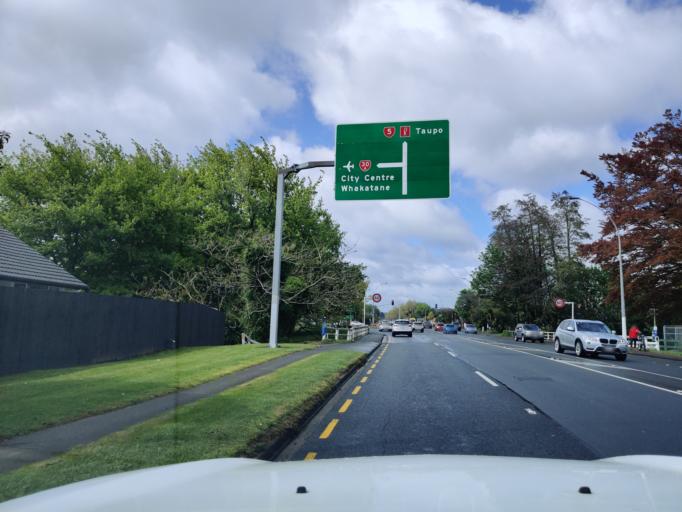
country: NZ
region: Bay of Plenty
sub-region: Rotorua District
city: Rotorua
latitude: -38.1356
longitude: 176.2350
